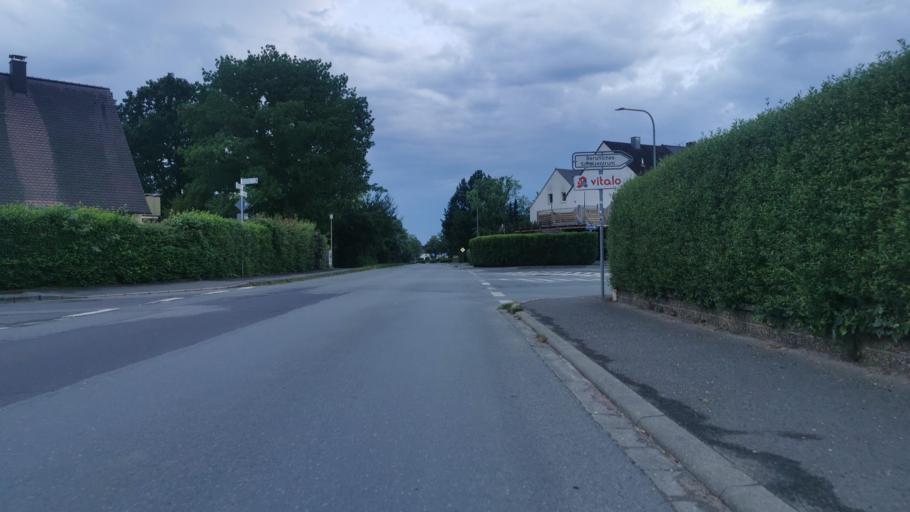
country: DE
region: Bavaria
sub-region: Regierungsbezirk Mittelfranken
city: Hochstadt an der Aisch
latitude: 49.7052
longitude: 10.8158
